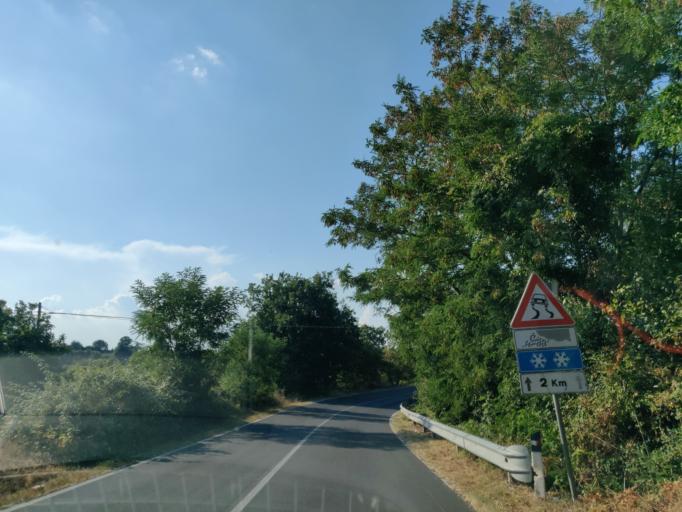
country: IT
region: Latium
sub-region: Provincia di Viterbo
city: Latera
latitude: 42.6399
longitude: 11.8382
